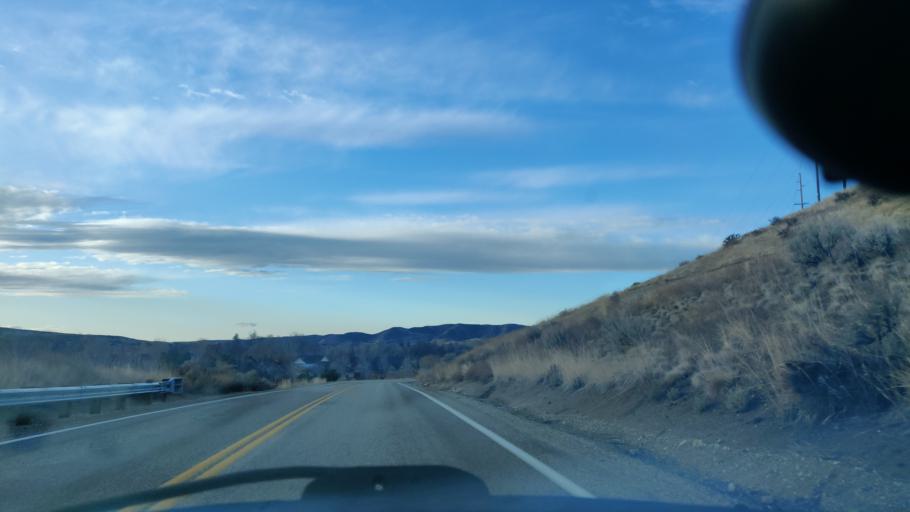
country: US
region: Idaho
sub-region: Ada County
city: Garden City
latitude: 43.7215
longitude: -116.2414
